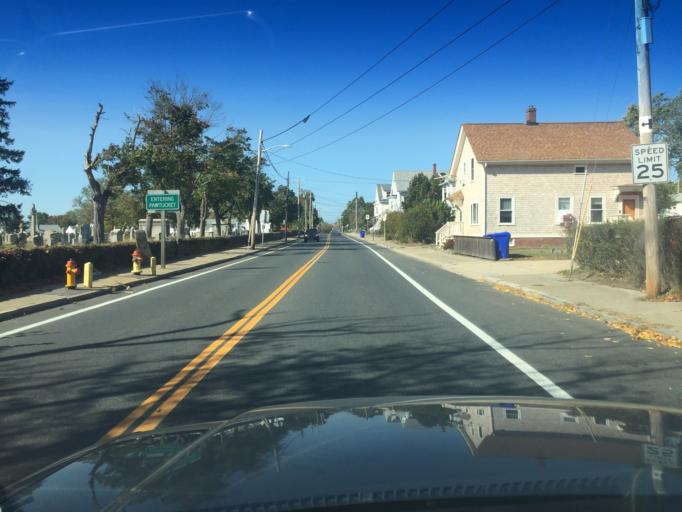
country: US
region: Rhode Island
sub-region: Providence County
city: Pawtucket
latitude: 41.8581
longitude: -71.3655
